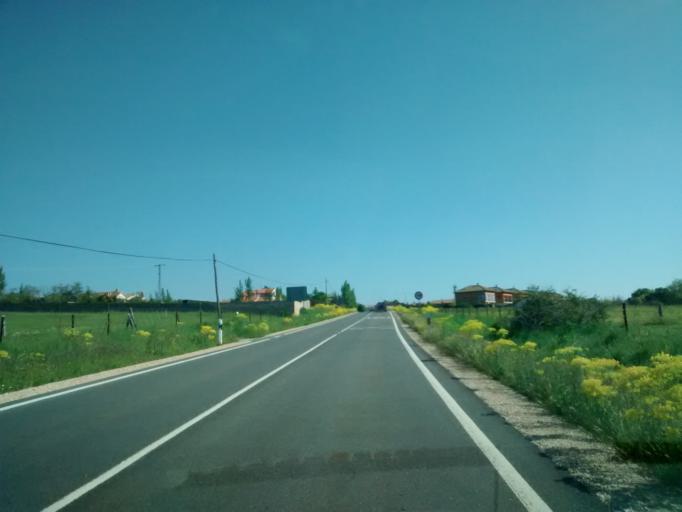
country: ES
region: Castille and Leon
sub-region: Provincia de Segovia
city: Torrecaballeros
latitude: 40.9874
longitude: -4.0239
